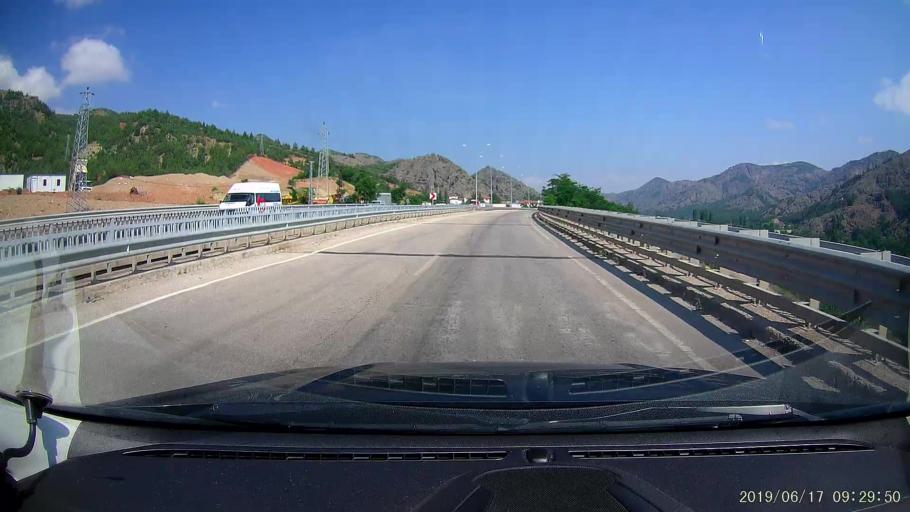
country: TR
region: Amasya
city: Amasya
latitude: 40.6996
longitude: 35.8075
